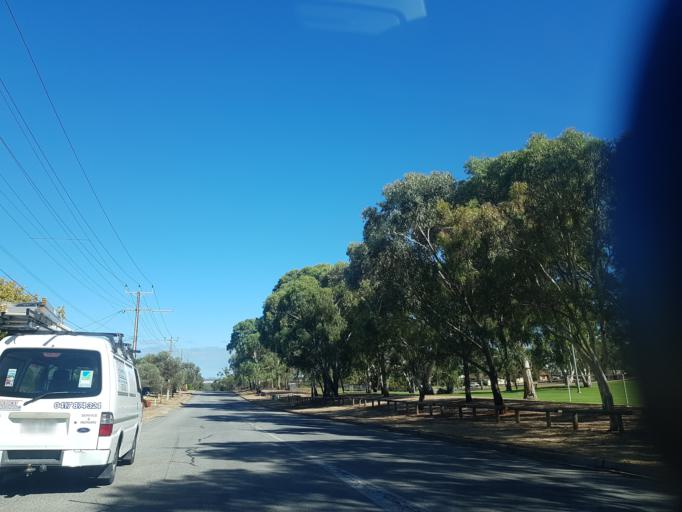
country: AU
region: South Australia
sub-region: Salisbury
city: Ingle Farm
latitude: -34.8275
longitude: 138.6532
